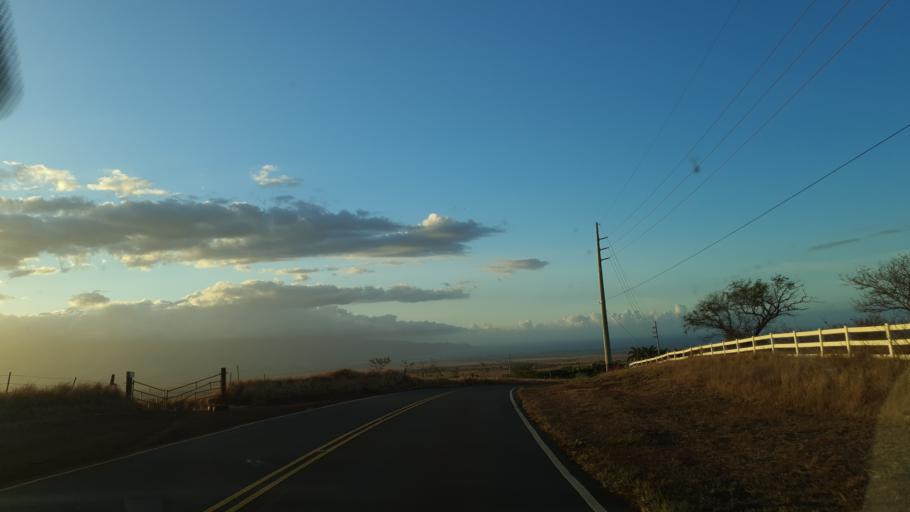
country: US
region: Hawaii
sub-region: Maui County
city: Pukalani
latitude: 20.7976
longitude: -156.3714
